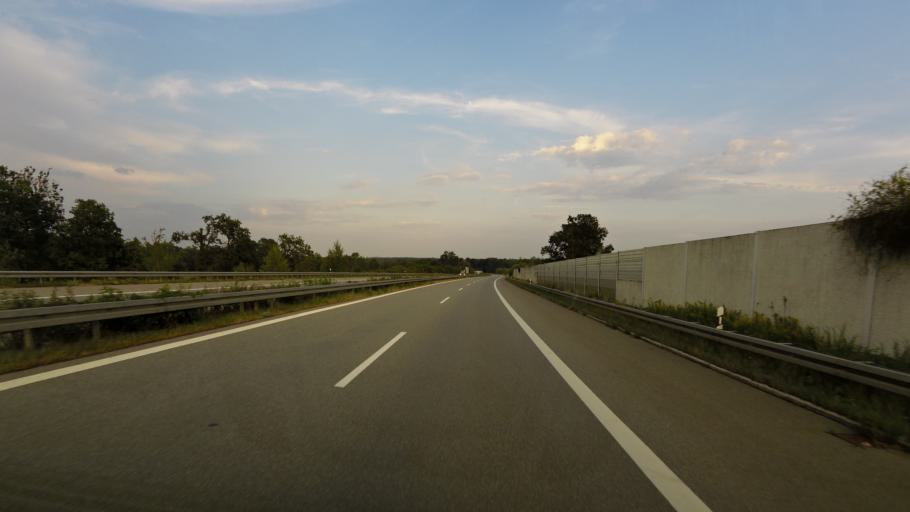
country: DE
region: Bavaria
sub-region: Upper Bavaria
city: Reischach
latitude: 48.2526
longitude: 12.7273
